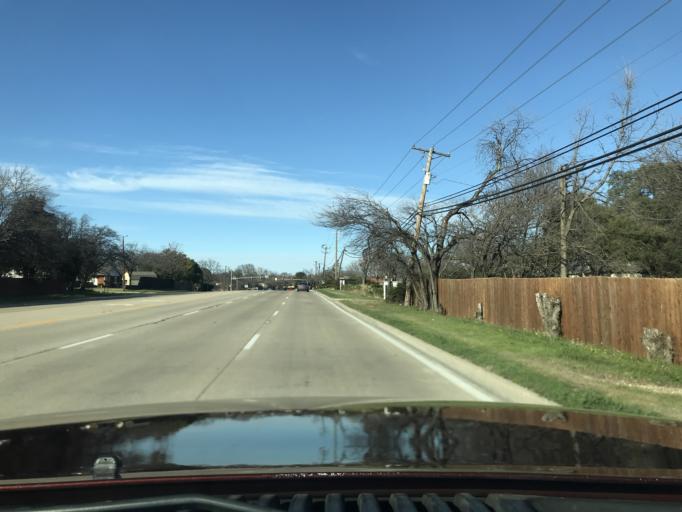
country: US
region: Texas
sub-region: Tarrant County
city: Edgecliff Village
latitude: 32.6593
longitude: -97.3485
